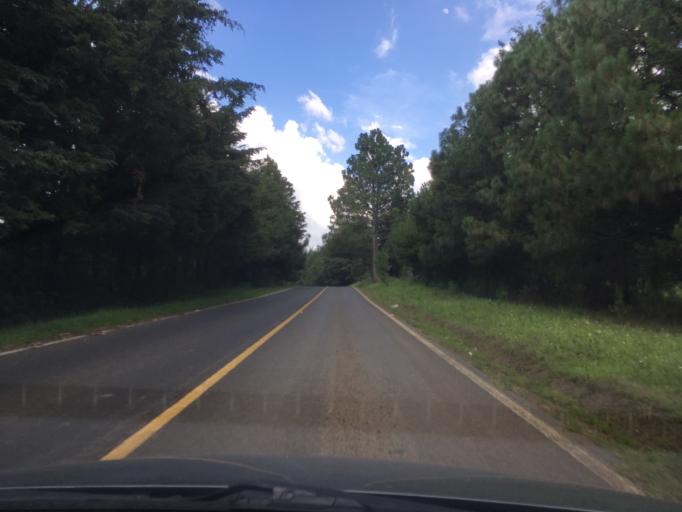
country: MX
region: Michoacan
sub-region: Nahuatzen
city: Sevina
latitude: 19.6167
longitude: -101.8773
